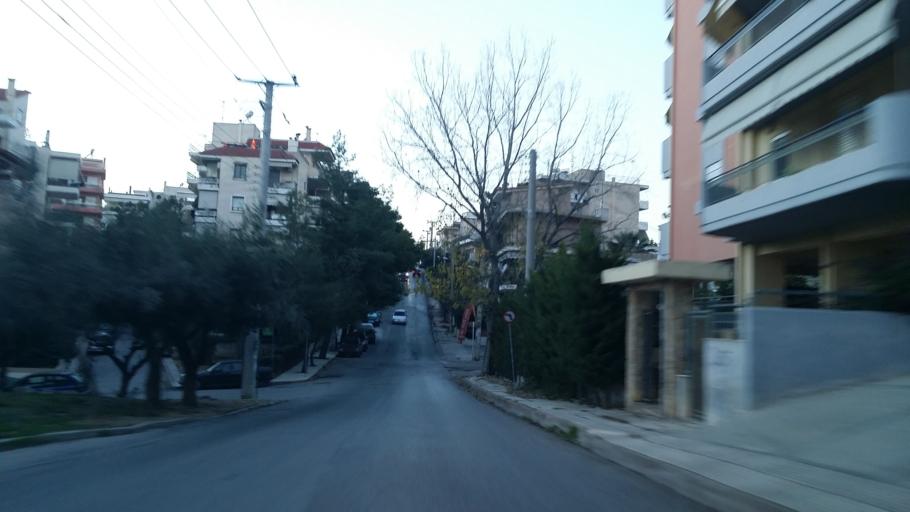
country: GR
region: Attica
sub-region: Nomarchia Athinas
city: Irakleio
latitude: 38.0536
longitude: 23.7638
